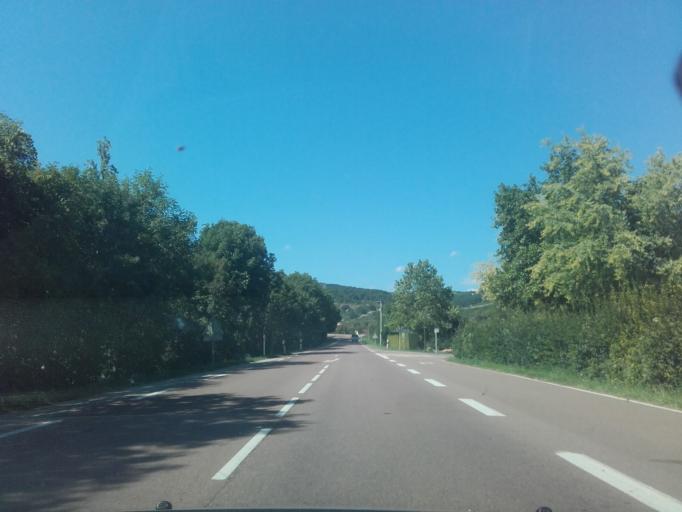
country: FR
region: Bourgogne
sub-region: Departement de la Cote-d'Or
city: Corpeau
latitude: 46.9499
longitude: 4.7259
